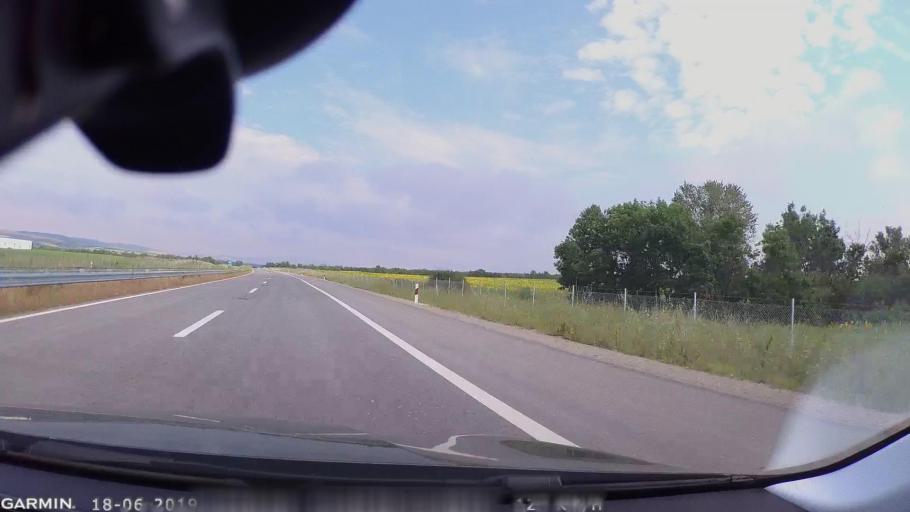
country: MK
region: Sveti Nikole
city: Sveti Nikole
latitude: 41.8275
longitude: 22.0049
